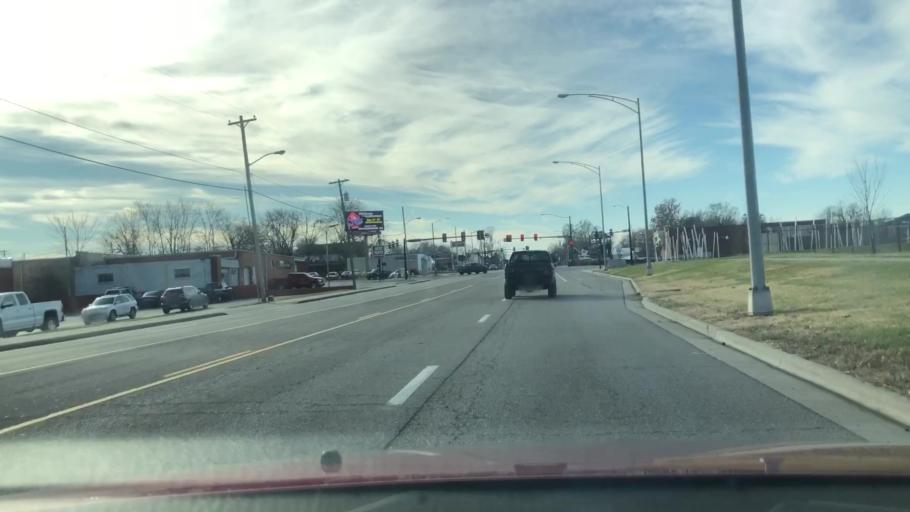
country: US
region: Missouri
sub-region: Greene County
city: Springfield
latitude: 37.2118
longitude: -93.2759
